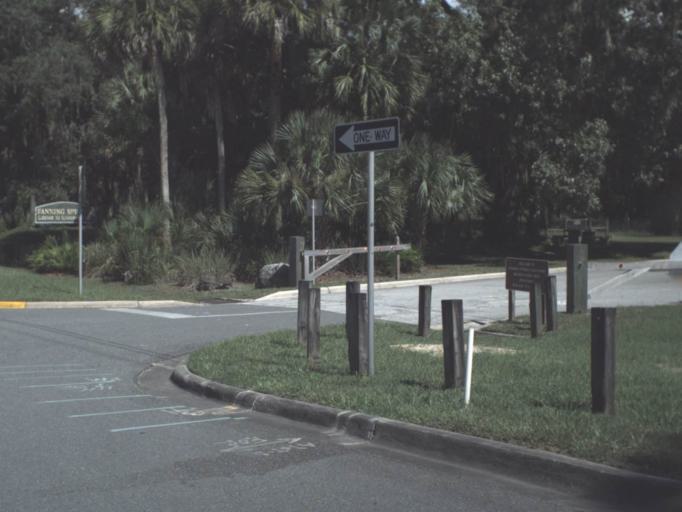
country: US
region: Florida
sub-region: Levy County
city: Manatee Road
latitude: 29.5910
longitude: -82.9360
